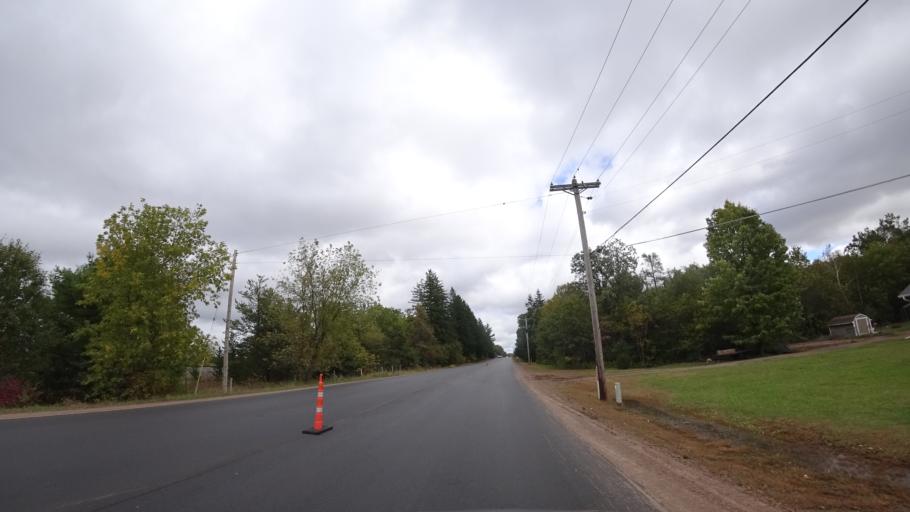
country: US
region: Wisconsin
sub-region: Chippewa County
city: Lake Wissota
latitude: 44.9295
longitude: -91.2829
